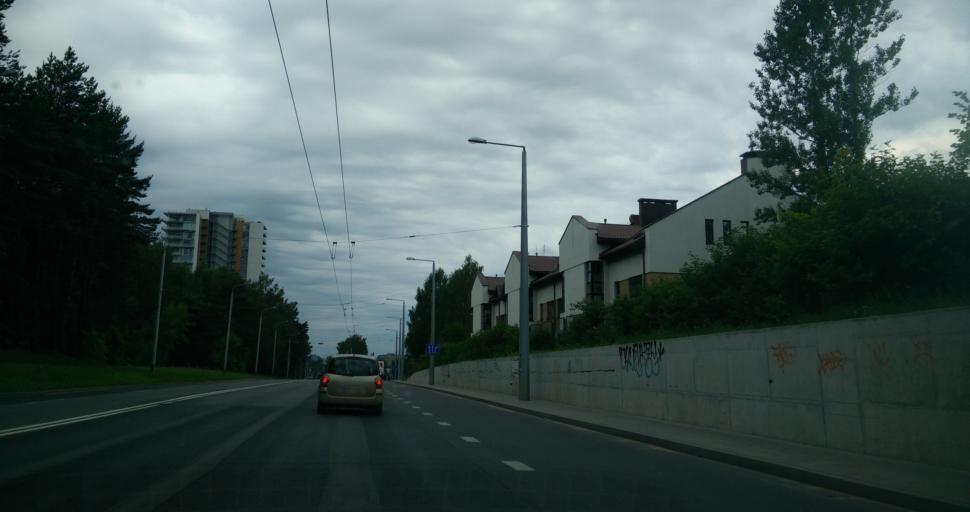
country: LT
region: Vilnius County
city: Rasos
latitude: 54.7260
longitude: 25.3246
